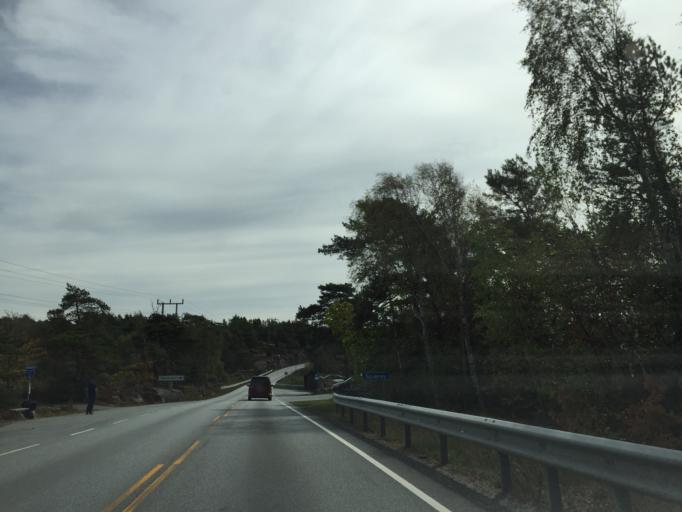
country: NO
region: Ostfold
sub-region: Fredrikstad
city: Fredrikstad
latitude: 59.0976
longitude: 10.9193
